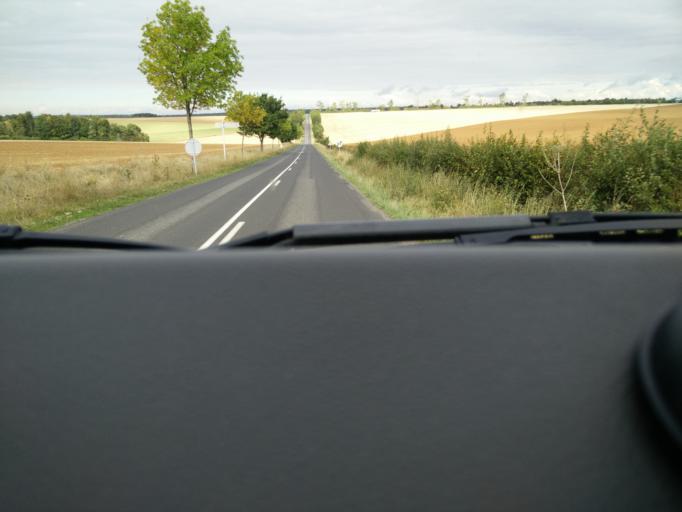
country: FR
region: Lorraine
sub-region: Departement de Meurthe-et-Moselle
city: Montauville
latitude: 48.9022
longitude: 5.9560
